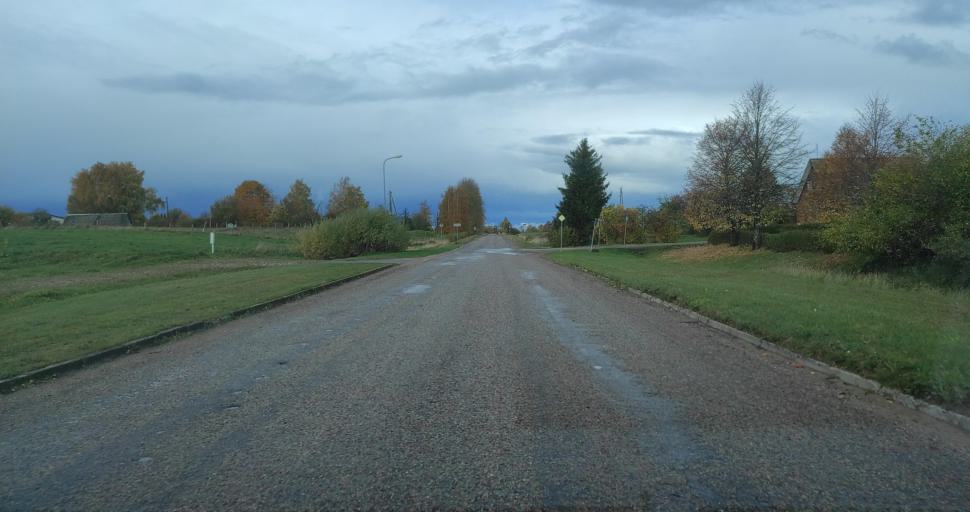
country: LV
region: Vainode
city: Vainode
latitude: 56.5718
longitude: 21.8958
